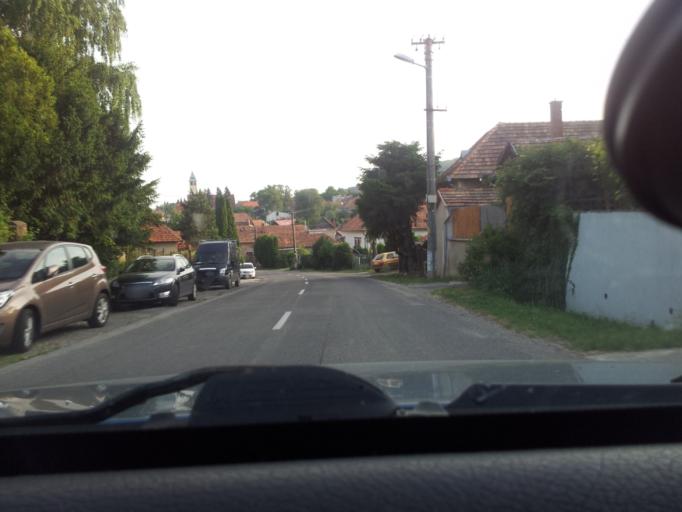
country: SK
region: Banskobystricky
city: Nova Bana
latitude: 48.3560
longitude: 18.7229
